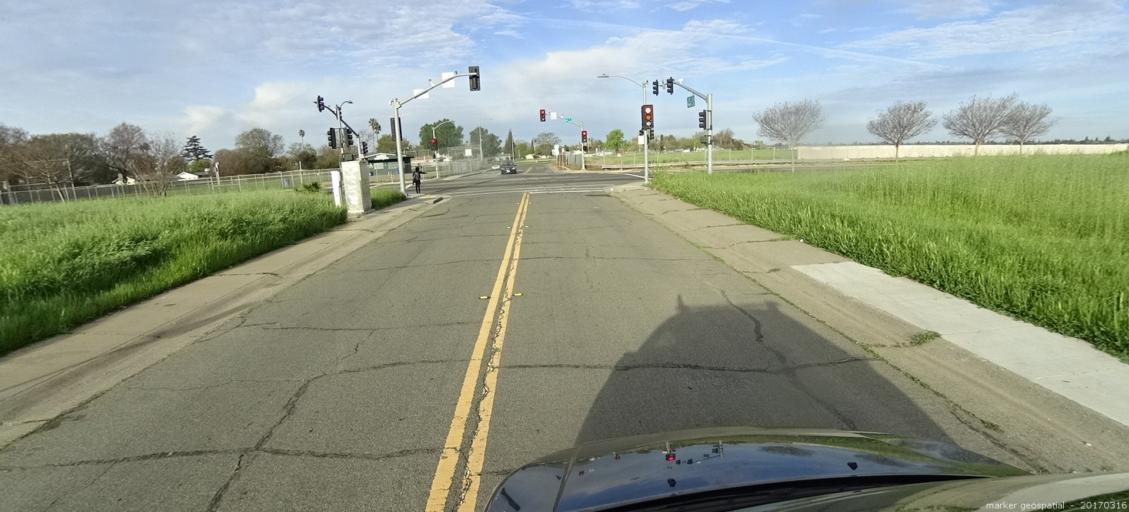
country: US
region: California
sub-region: Sacramento County
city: Parkway
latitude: 38.5091
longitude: -121.4824
